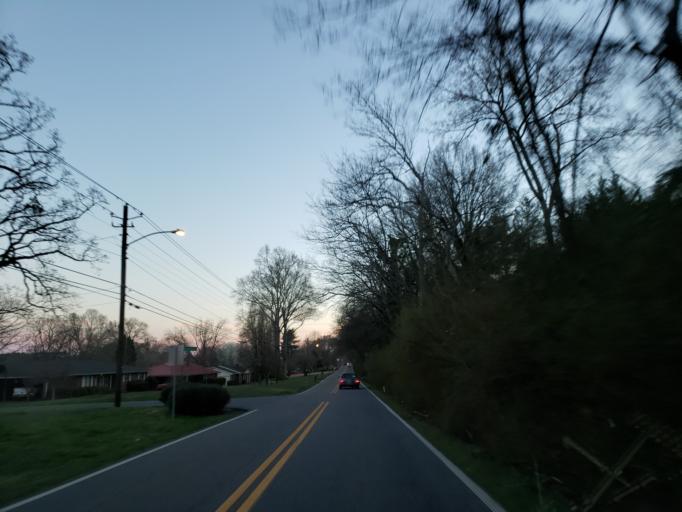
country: US
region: Georgia
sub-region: Bartow County
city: Cartersville
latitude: 34.2049
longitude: -84.8195
